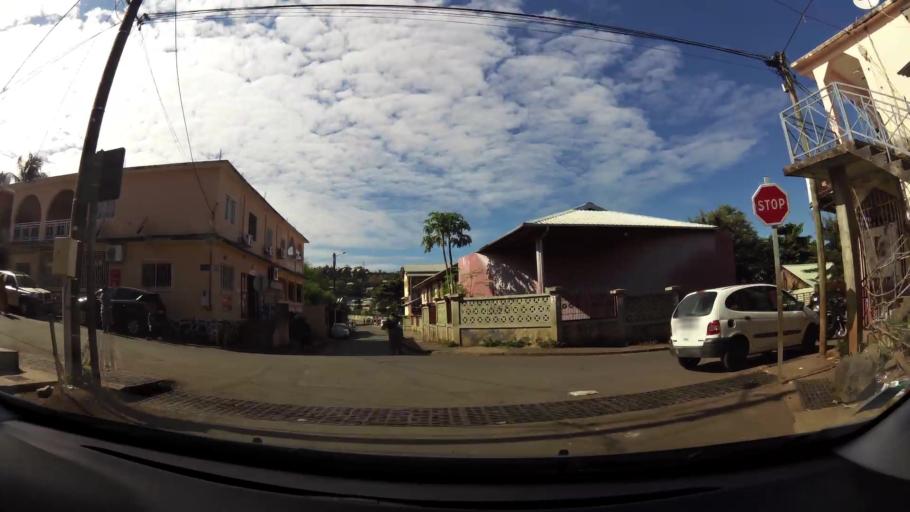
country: YT
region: Mamoudzou
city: Mamoudzou
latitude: -12.7846
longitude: 45.2198
